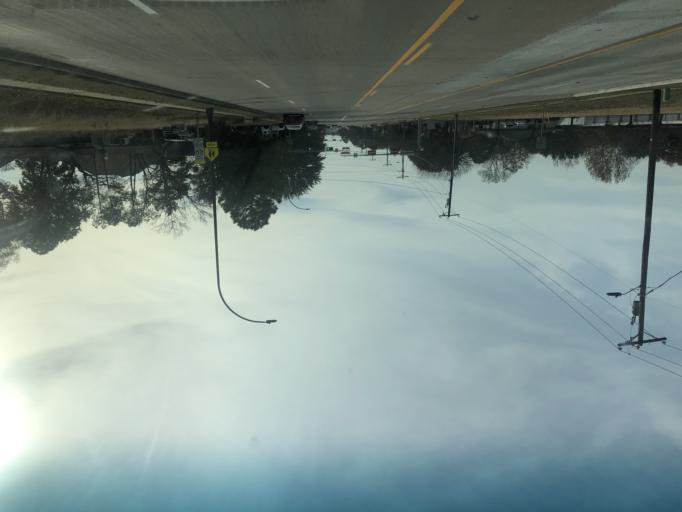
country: US
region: Texas
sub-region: Tarrant County
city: Dalworthington Gardens
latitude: 32.6872
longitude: -97.1494
